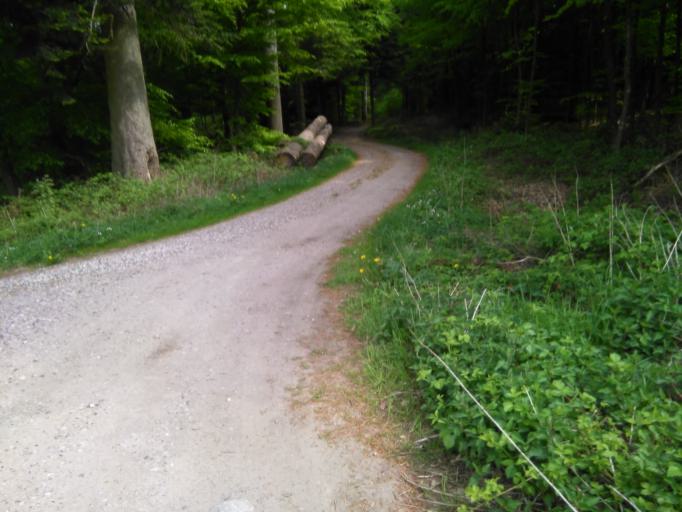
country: DK
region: Central Jutland
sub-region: Horsens Kommune
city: Braedstrup
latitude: 56.0481
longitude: 9.6135
